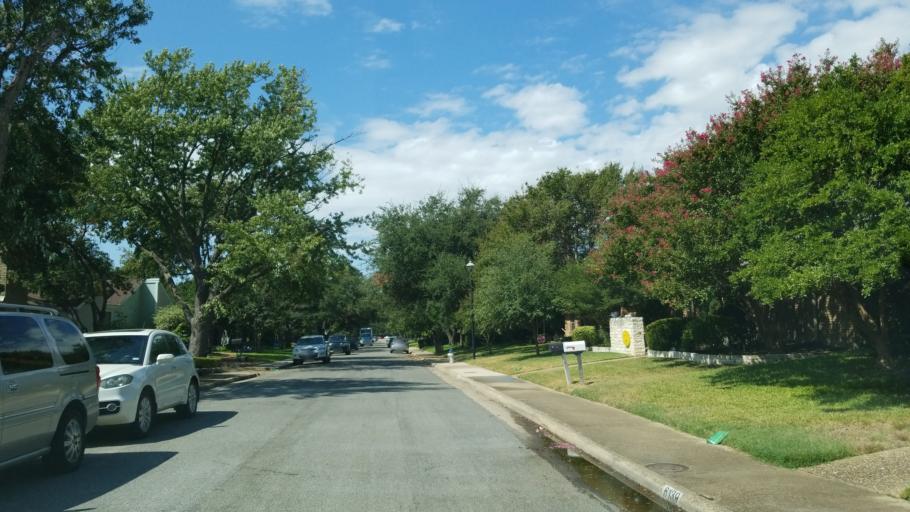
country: US
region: Texas
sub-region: Dallas County
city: Addison
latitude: 32.9571
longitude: -96.8000
